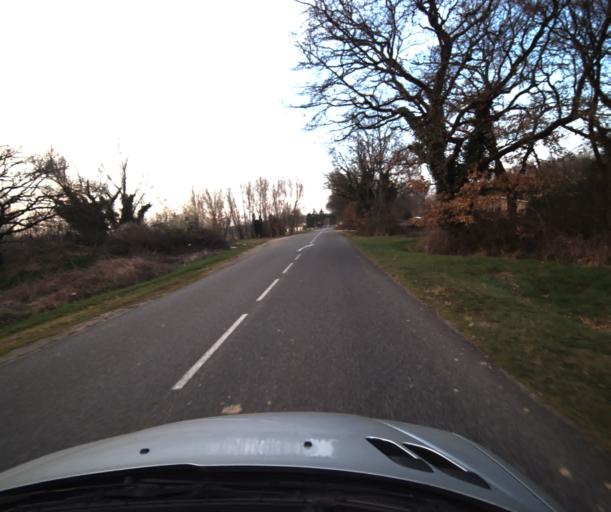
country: FR
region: Midi-Pyrenees
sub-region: Departement du Tarn-et-Garonne
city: Labastide-Saint-Pierre
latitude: 43.9019
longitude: 1.3694
